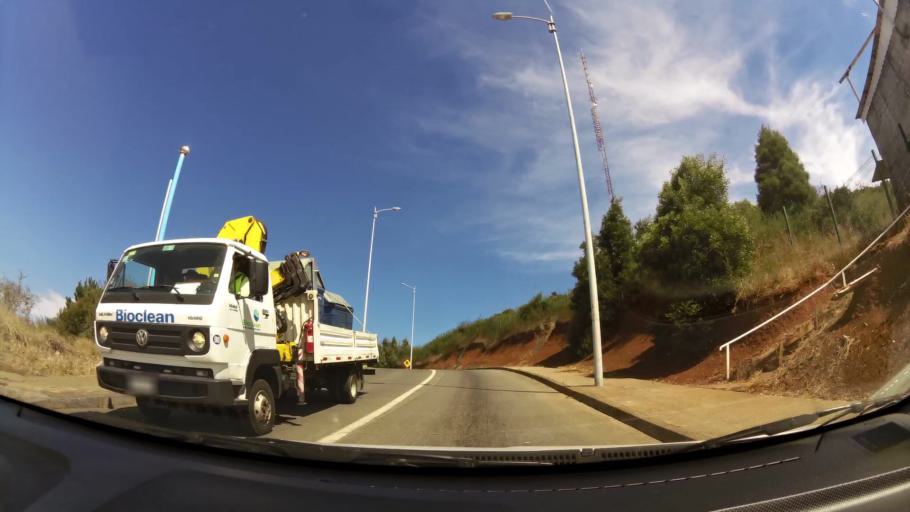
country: CL
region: Biobio
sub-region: Provincia de Concepcion
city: Talcahuano
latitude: -36.7079
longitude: -73.1225
